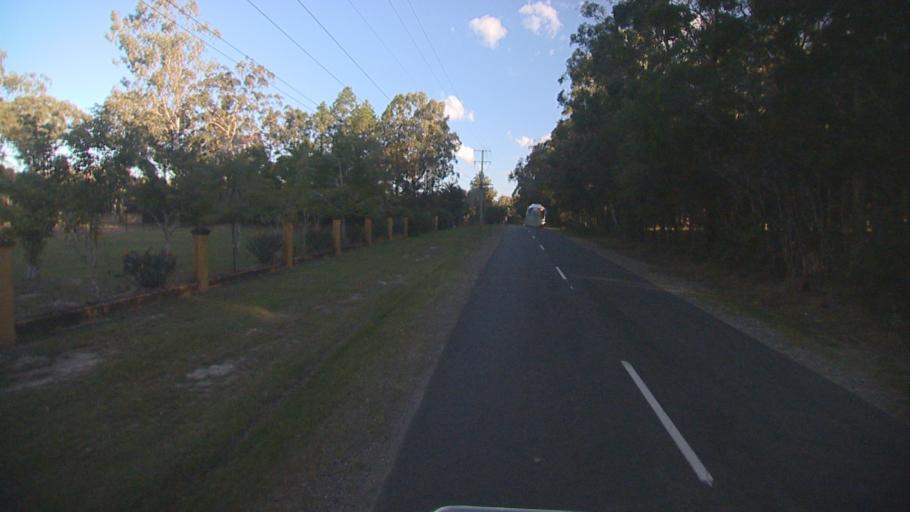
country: AU
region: Queensland
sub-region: Gold Coast
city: Yatala
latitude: -27.6831
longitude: 153.2747
